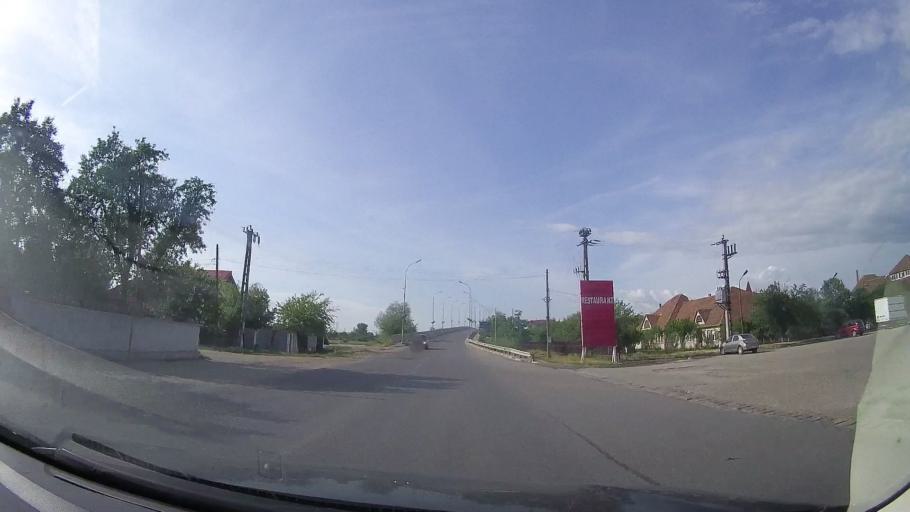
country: RO
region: Caras-Severin
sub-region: Comuna Buchin
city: Buchin
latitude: 45.3823
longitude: 22.2318
